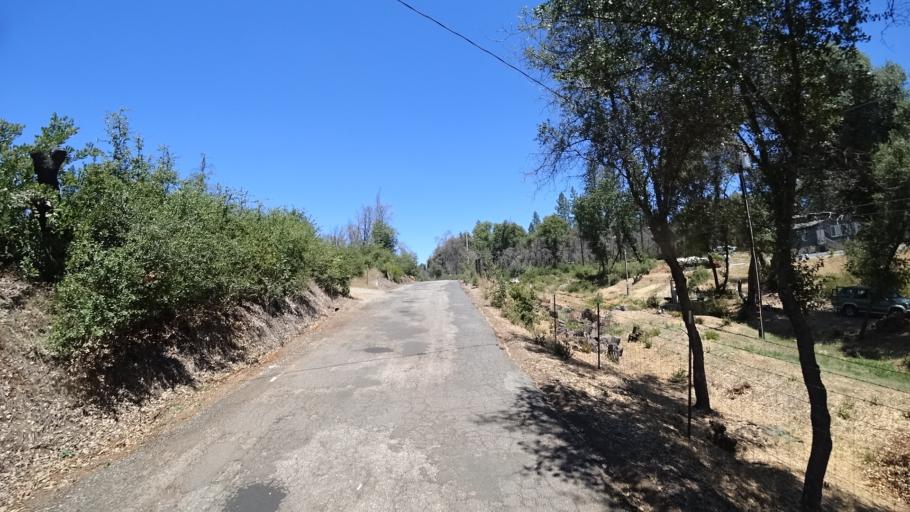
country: US
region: California
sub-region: Calaveras County
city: Mountain Ranch
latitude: 38.2366
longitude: -120.5466
